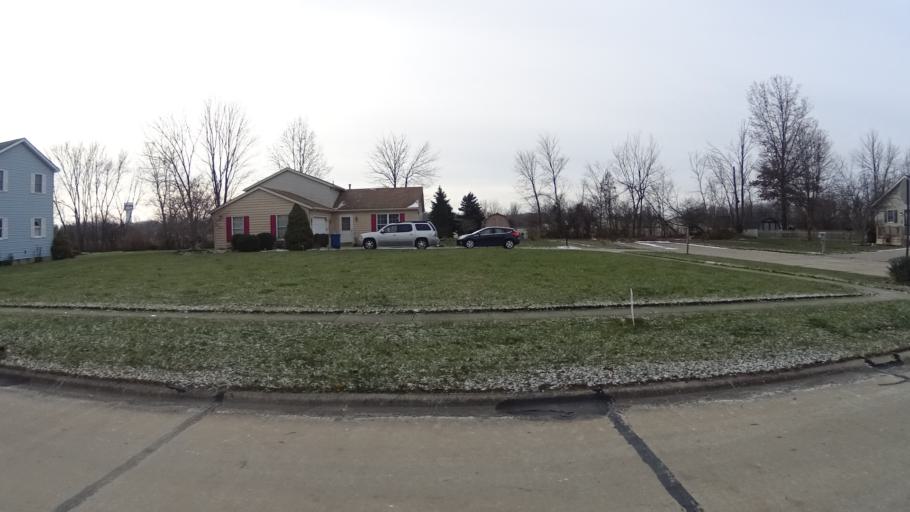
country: US
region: Ohio
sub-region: Lorain County
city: Lagrange
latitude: 41.2453
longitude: -82.1270
